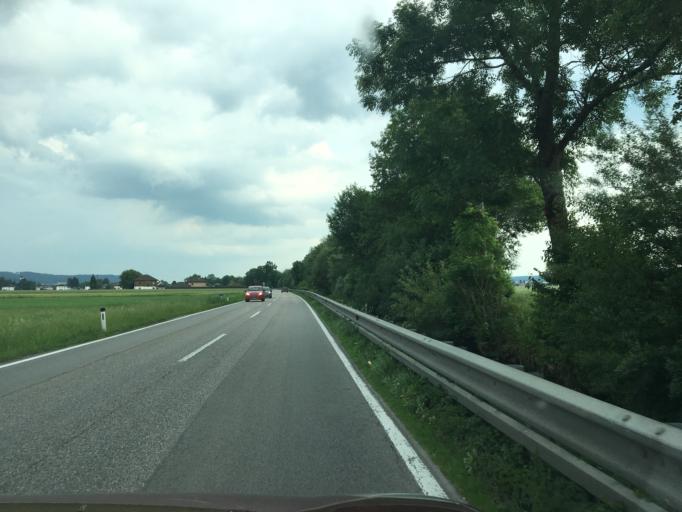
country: AT
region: Upper Austria
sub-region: Politischer Bezirk Braunau am Inn
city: Altheim
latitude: 48.1291
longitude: 13.1473
